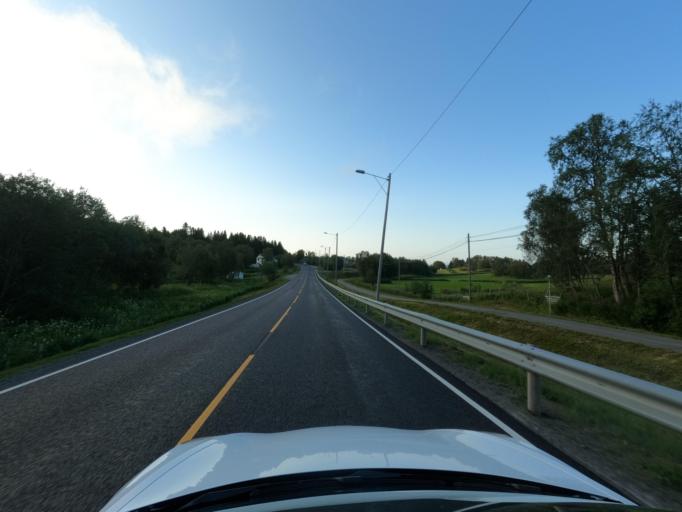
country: NO
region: Troms
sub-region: Skanland
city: Evenskjer
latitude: 68.6670
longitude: 16.5759
